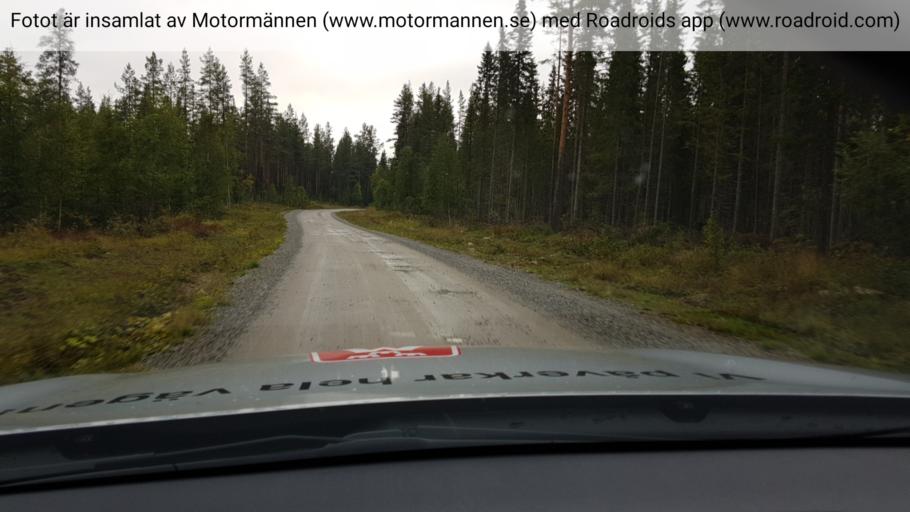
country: SE
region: Jaemtland
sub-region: Braecke Kommun
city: Braecke
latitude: 62.7454
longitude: 15.5027
